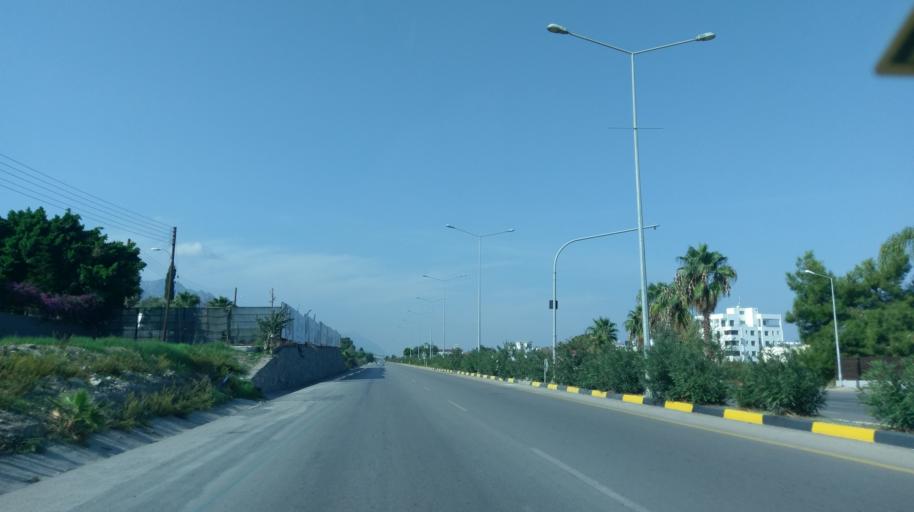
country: CY
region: Keryneia
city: Kyrenia
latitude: 35.3275
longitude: 33.3089
